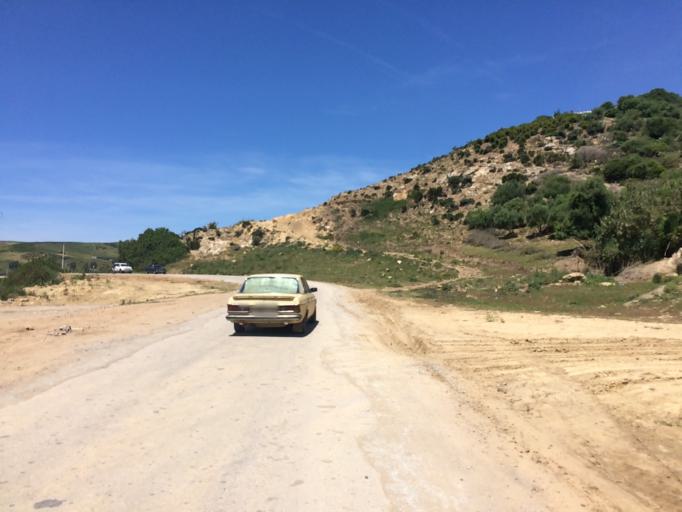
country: MA
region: Tanger-Tetouan
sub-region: Larache
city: Larache
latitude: 35.1987
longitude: -6.0845
